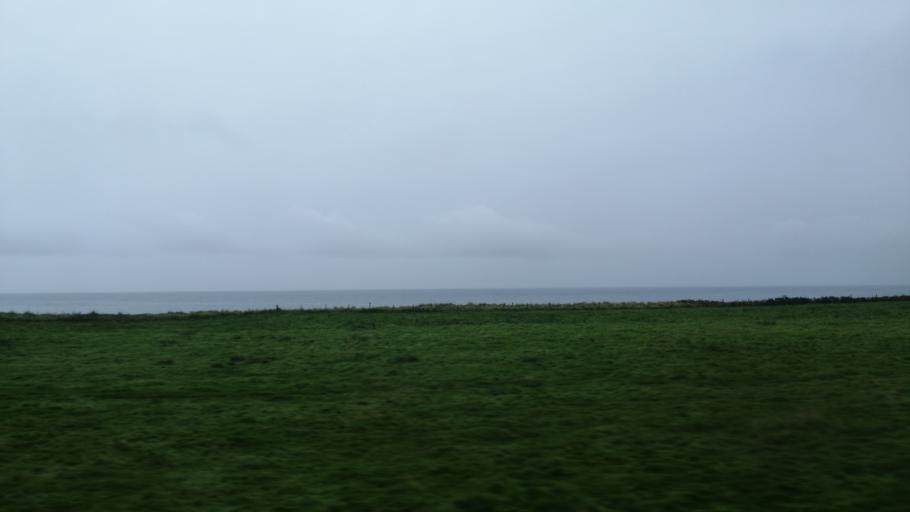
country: GB
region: Scotland
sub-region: Highland
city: Brora
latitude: 58.0440
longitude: -3.8230
